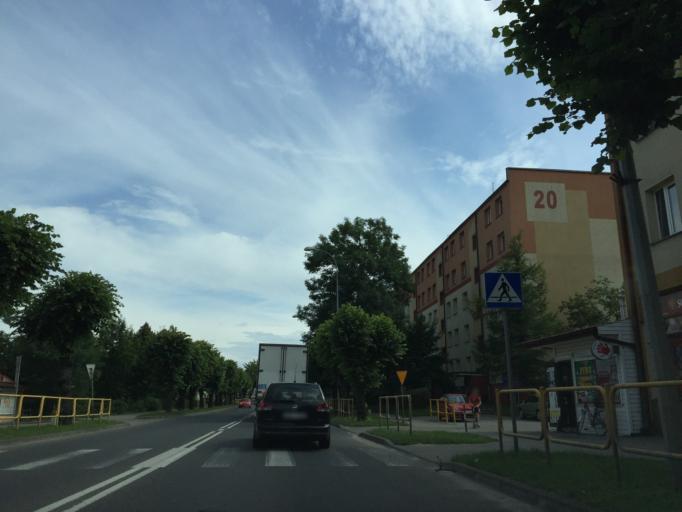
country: PL
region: Podlasie
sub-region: Powiat siemiatycki
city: Siemiatycze
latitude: 52.4273
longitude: 22.8635
